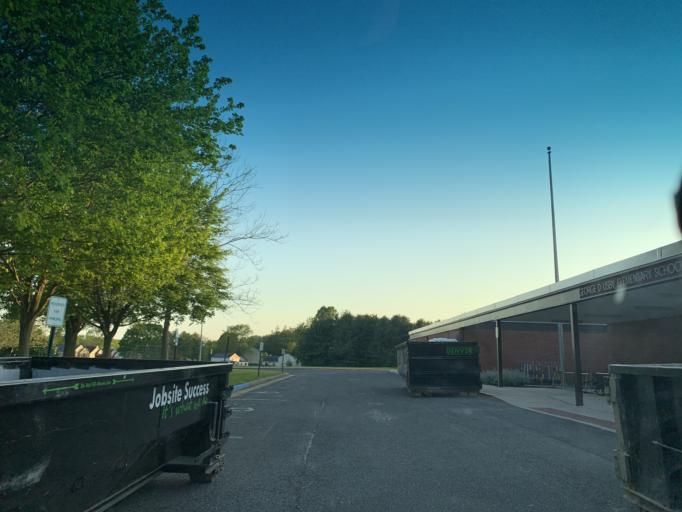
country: US
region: Maryland
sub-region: Harford County
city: Aberdeen
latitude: 39.5035
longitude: -76.1797
